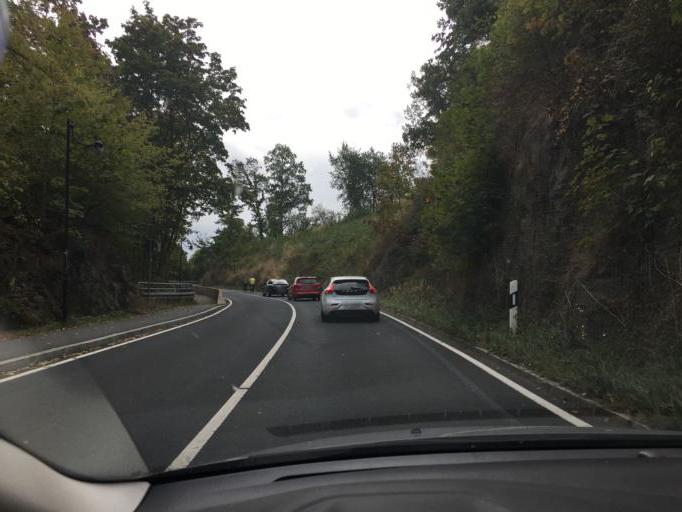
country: DE
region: Thuringia
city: Birkenhugel
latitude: 50.4973
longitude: 11.7279
